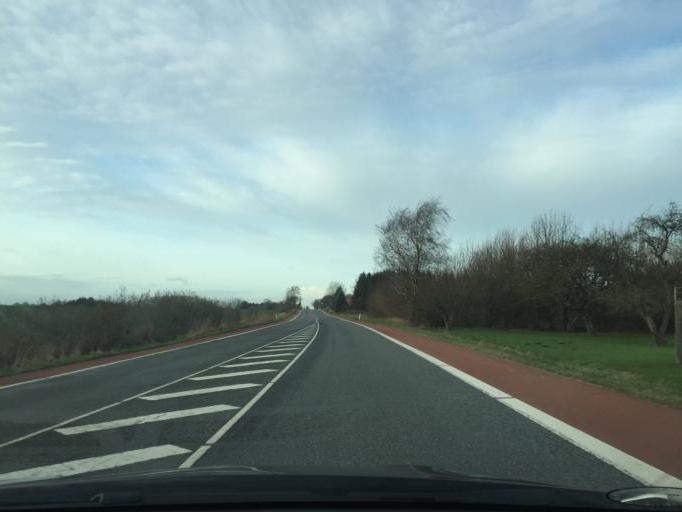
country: DK
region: South Denmark
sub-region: Faaborg-Midtfyn Kommune
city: Ringe
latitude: 55.2627
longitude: 10.4617
